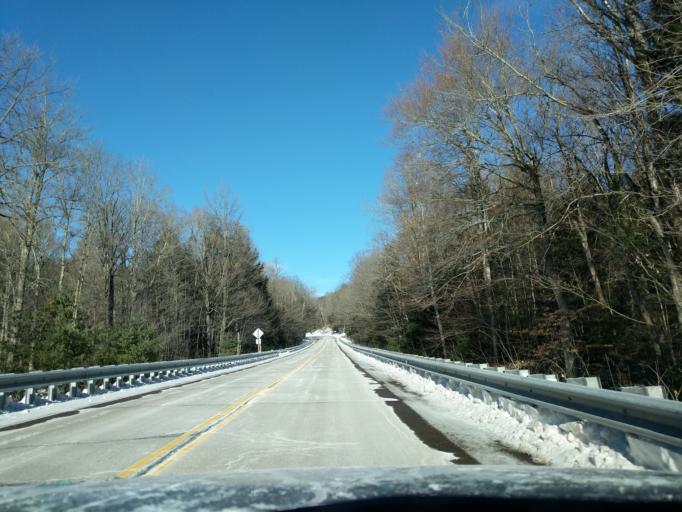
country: US
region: Wisconsin
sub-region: Menominee County
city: Keshena
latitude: 45.0948
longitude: -88.6341
